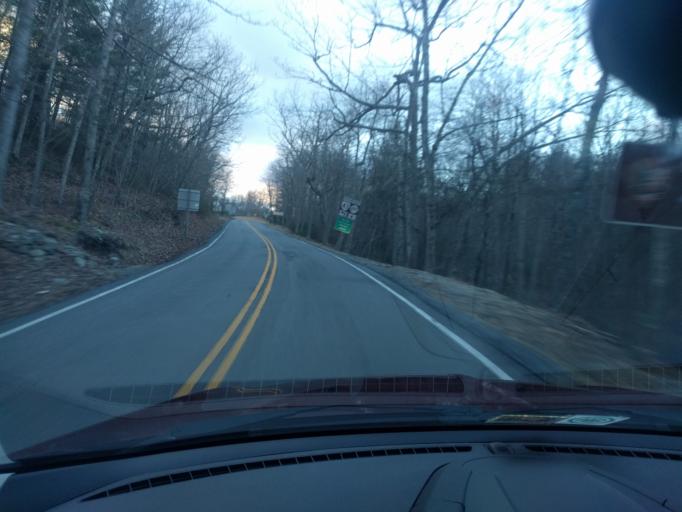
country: US
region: Virginia
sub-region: Botetourt County
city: Buchanan
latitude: 37.4857
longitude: -79.6685
